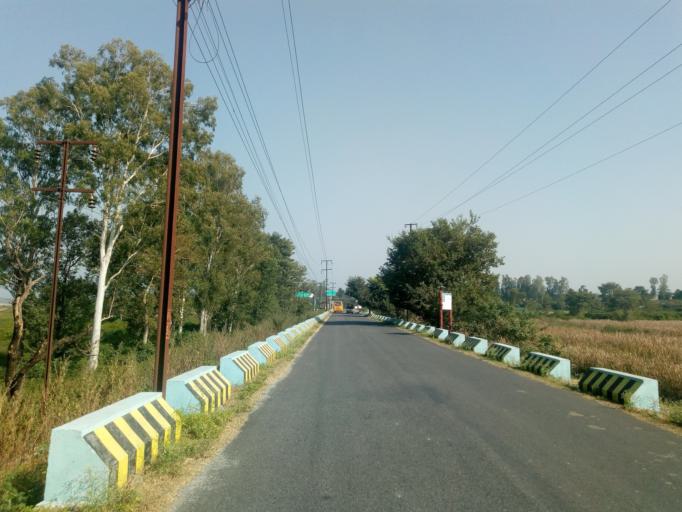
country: IN
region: Himachal Pradesh
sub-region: Sirmaur
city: Paonta Sahib
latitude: 30.4421
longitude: 77.6748
